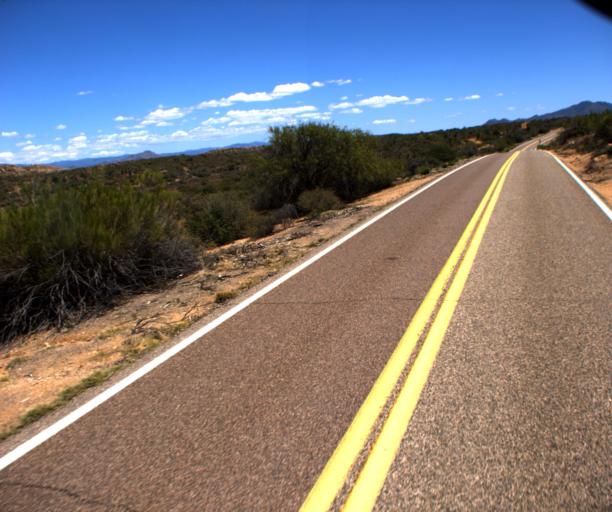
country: US
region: Arizona
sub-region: Yavapai County
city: Bagdad
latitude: 34.4408
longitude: -112.9327
